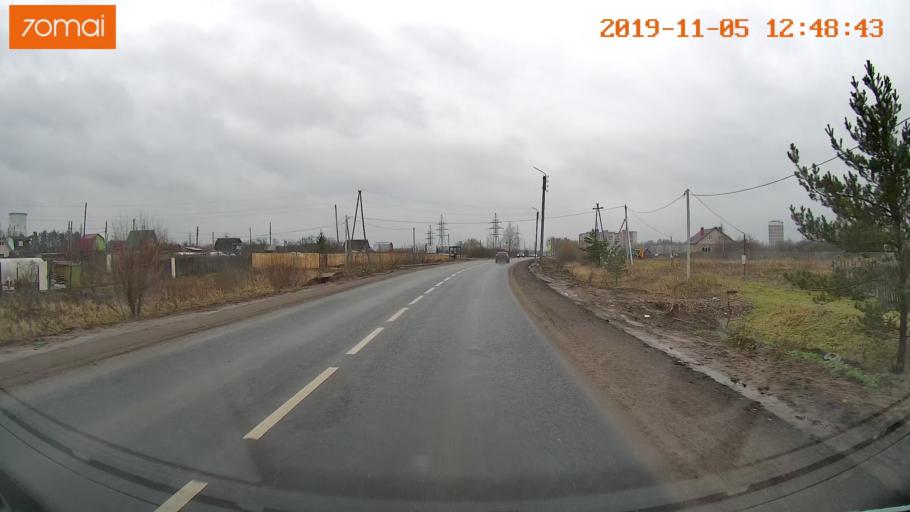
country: RU
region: Ivanovo
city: Kokhma
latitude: 56.9590
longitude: 41.1003
